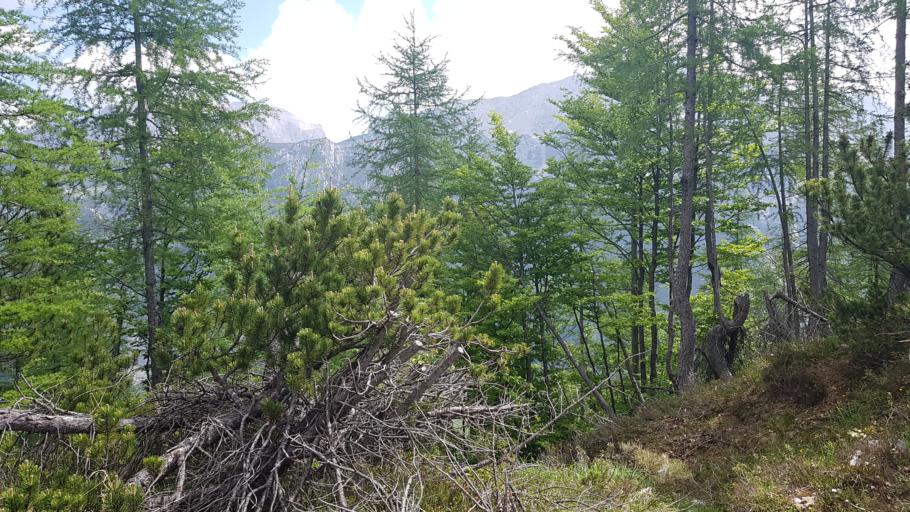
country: IT
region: Friuli Venezia Giulia
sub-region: Provincia di Udine
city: Paularo
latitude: 46.5348
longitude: 13.1926
